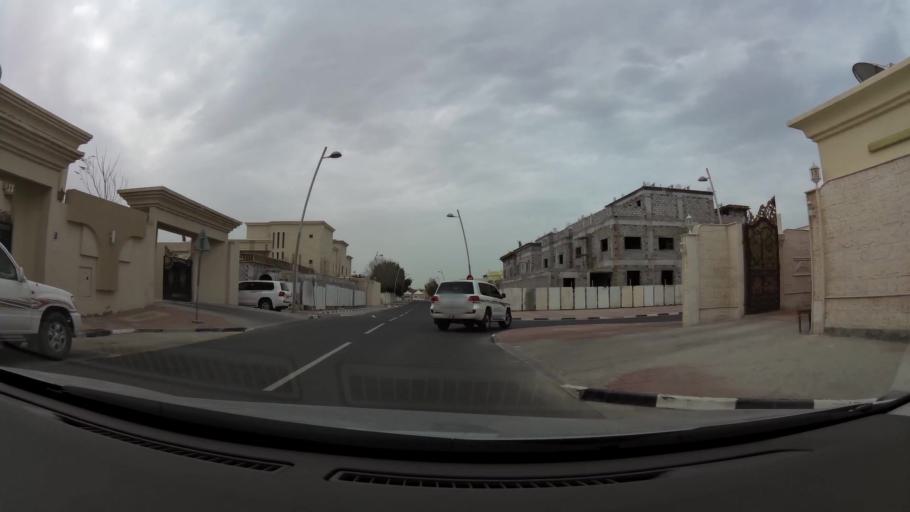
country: QA
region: Baladiyat ad Dawhah
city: Doha
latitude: 25.3395
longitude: 51.4871
